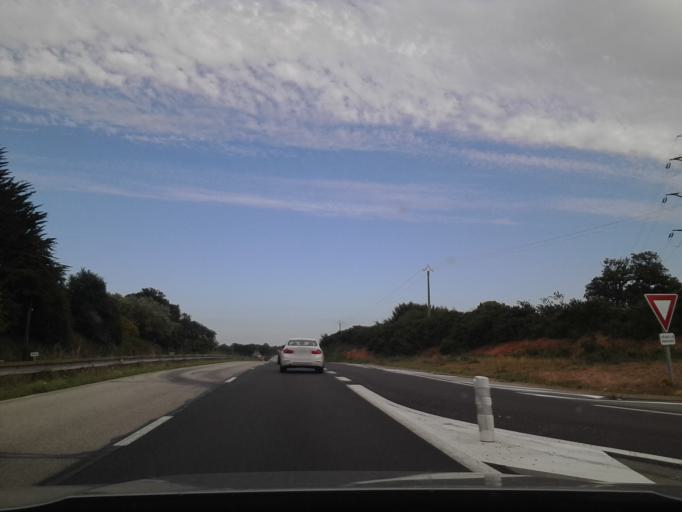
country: FR
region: Lower Normandy
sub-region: Departement de la Manche
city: La Glacerie
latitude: 49.5833
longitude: -1.5912
